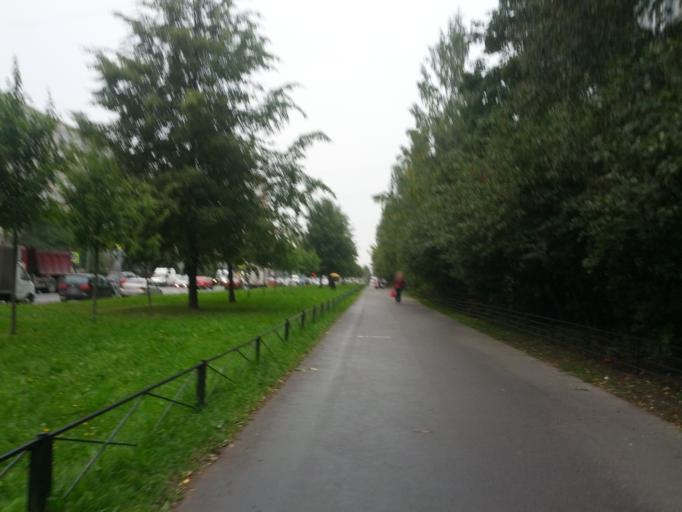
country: RU
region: St.-Petersburg
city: Obukhovo
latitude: 59.9011
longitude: 30.4715
